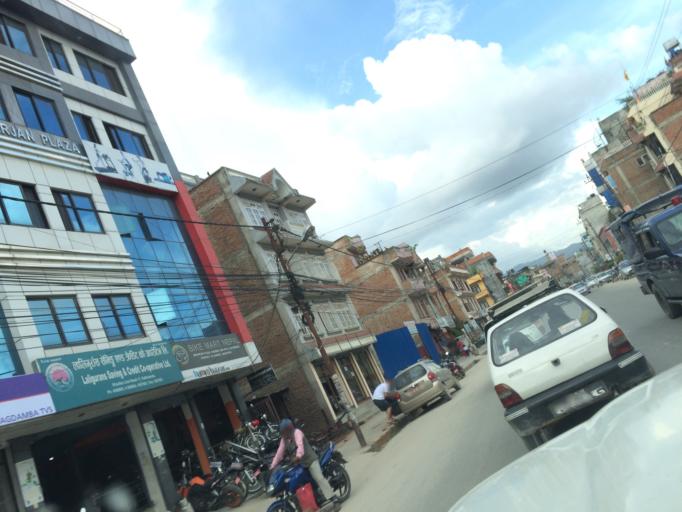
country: NP
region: Central Region
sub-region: Bagmati Zone
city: Kathmandu
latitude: 27.7168
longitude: 85.3044
